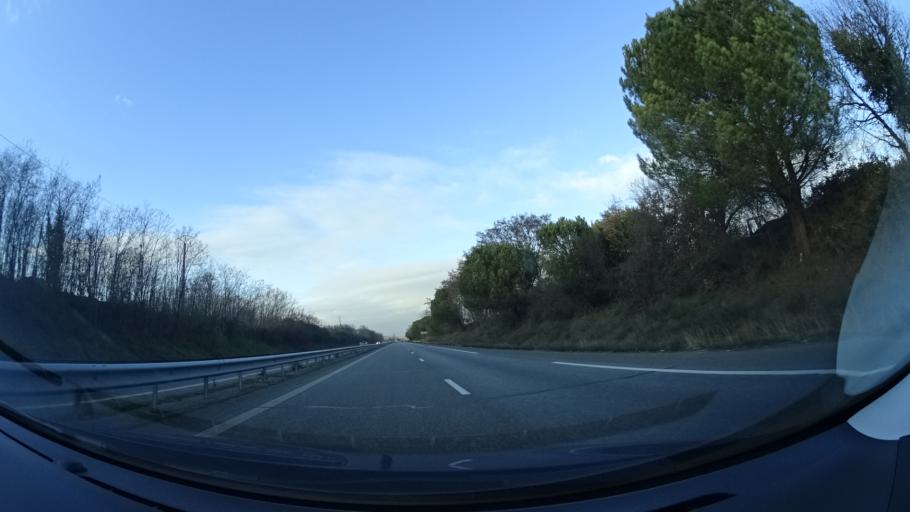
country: FR
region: Midi-Pyrenees
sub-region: Departement de l'Ariege
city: Saint-Jean-du-Falga
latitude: 43.0823
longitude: 1.6367
